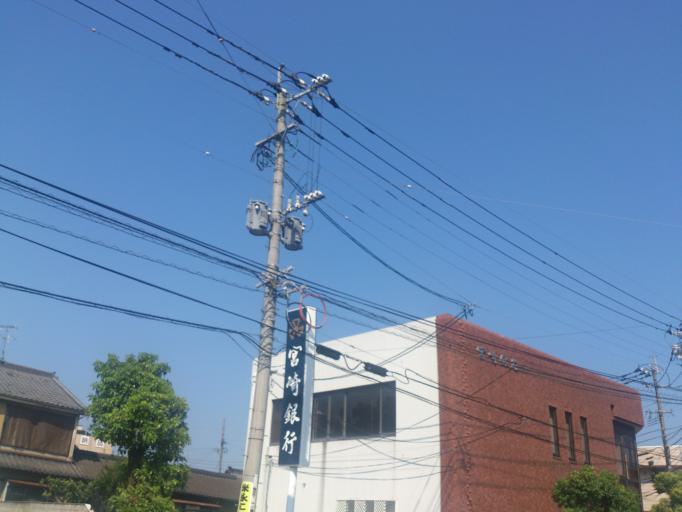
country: JP
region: Kagoshima
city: Kanoya
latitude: 31.3903
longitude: 130.8503
